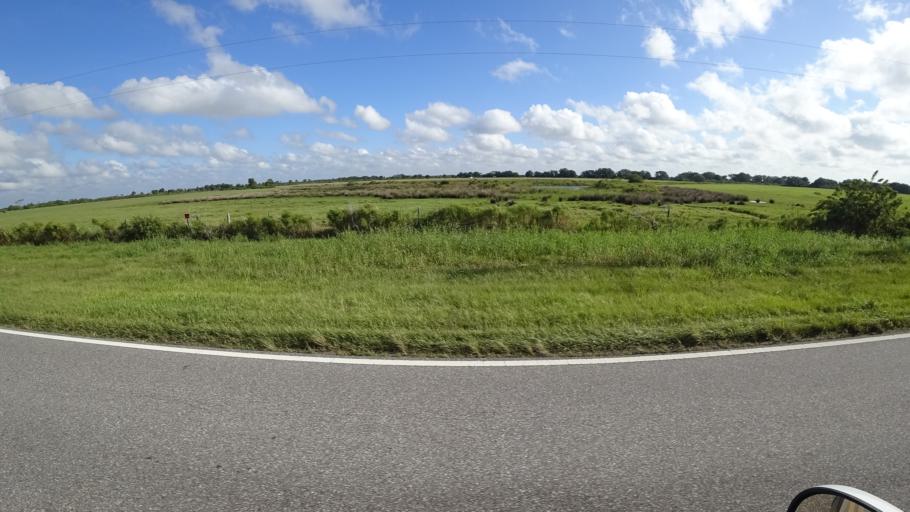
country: US
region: Florida
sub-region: Hillsborough County
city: Wimauma
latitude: 27.5150
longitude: -82.3240
